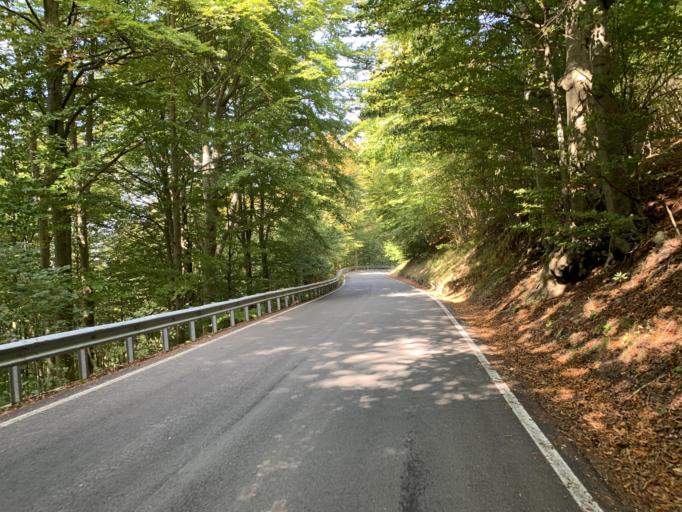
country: IT
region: Liguria
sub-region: Provincia di Savona
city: Osiglia
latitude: 44.2323
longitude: 8.1960
